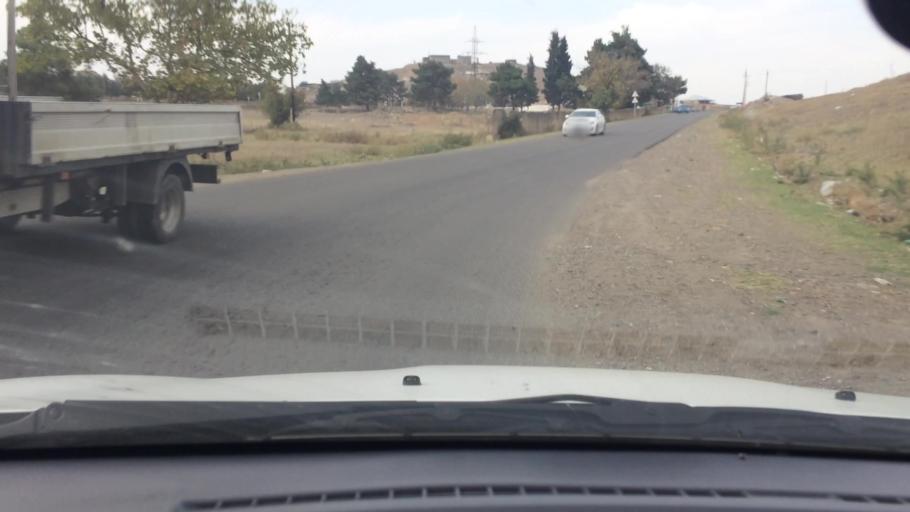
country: GE
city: Naghvarevi
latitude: 41.3608
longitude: 44.8371
